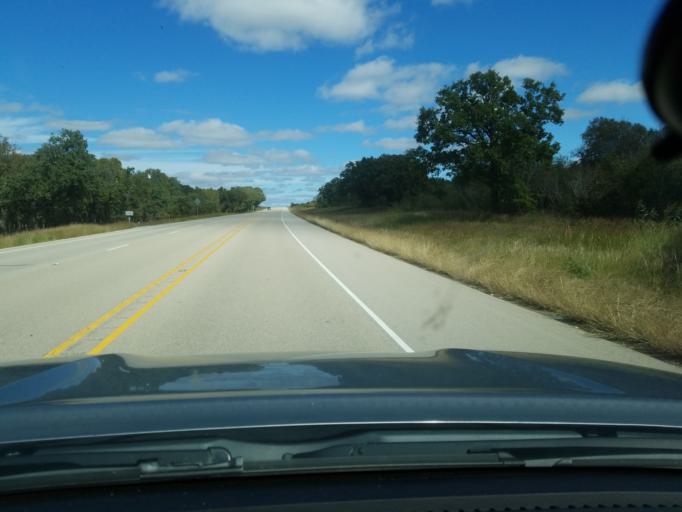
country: US
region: Texas
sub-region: Hamilton County
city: Hamilton
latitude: 31.6181
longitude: -98.1581
